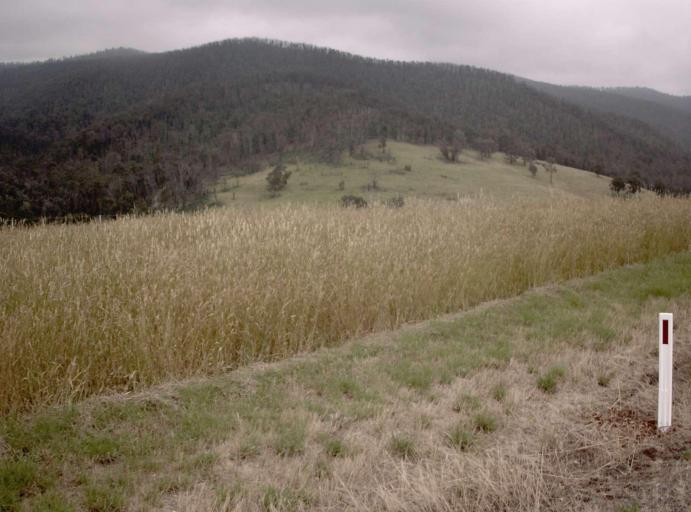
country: AU
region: Victoria
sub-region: Wellington
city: Heyfield
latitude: -37.8337
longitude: 146.6795
